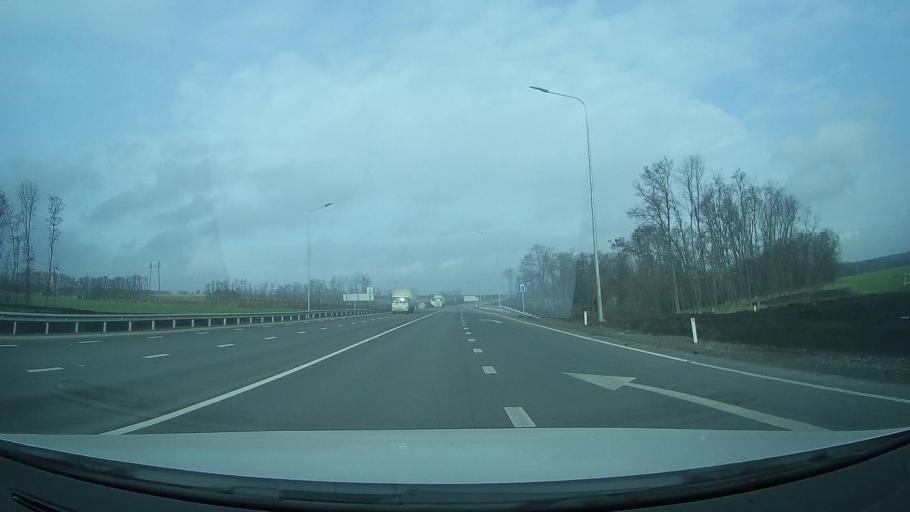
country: RU
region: Rostov
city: Grushevskaya
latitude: 47.3821
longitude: 39.8454
